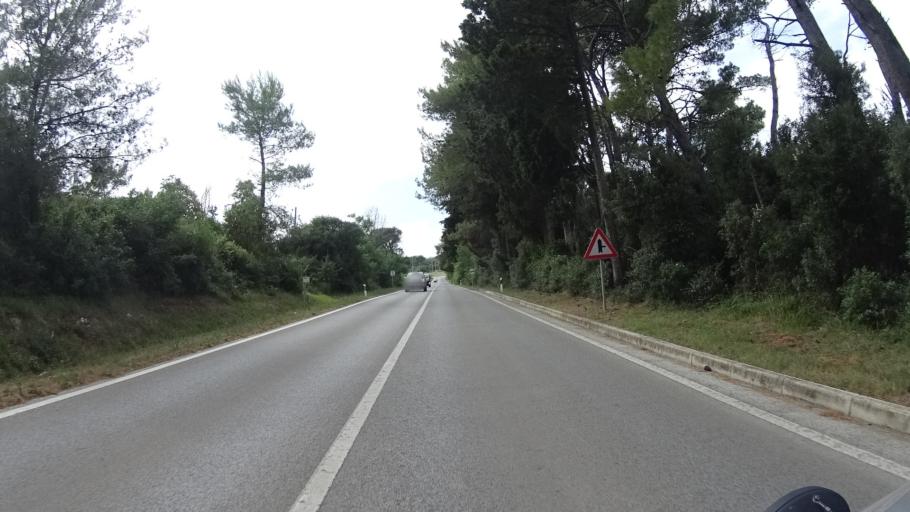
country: HR
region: Istarska
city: Medulin
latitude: 44.8184
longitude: 13.8855
